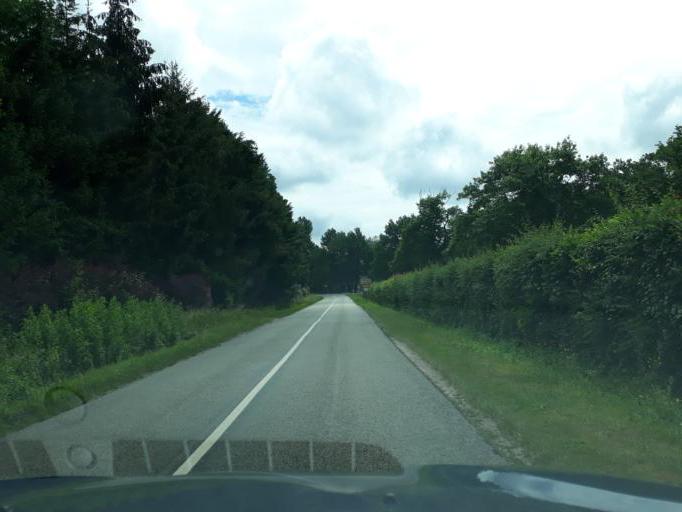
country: FR
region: Centre
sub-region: Departement du Loir-et-Cher
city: Chaumont-sur-Tharonne
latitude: 47.6134
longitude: 1.8980
